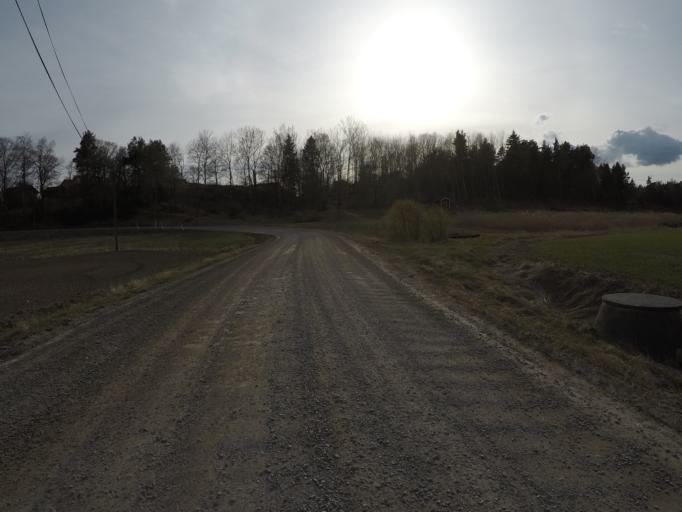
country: SE
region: Soedermanland
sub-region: Eskilstuna Kommun
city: Eskilstuna
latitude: 59.4353
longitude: 16.5605
